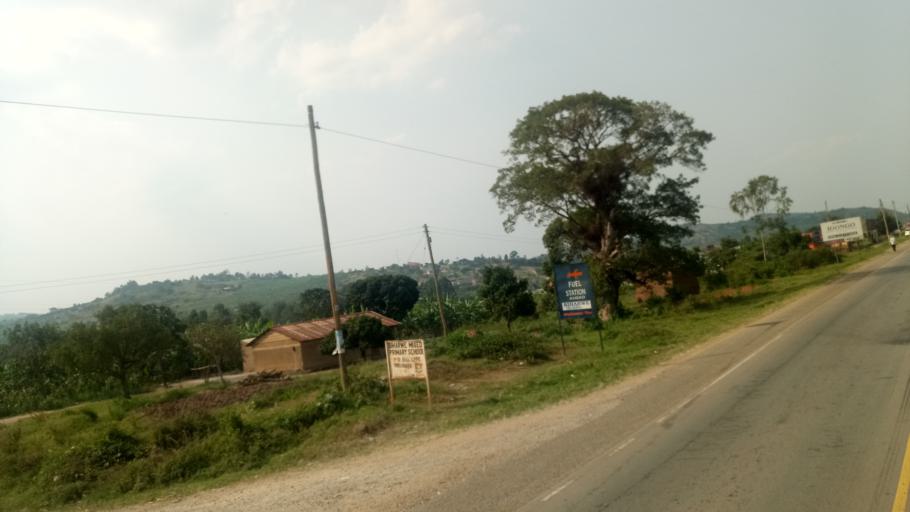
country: UG
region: Western Region
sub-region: Mbarara District
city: Mbarara
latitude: -0.5267
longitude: 30.7276
